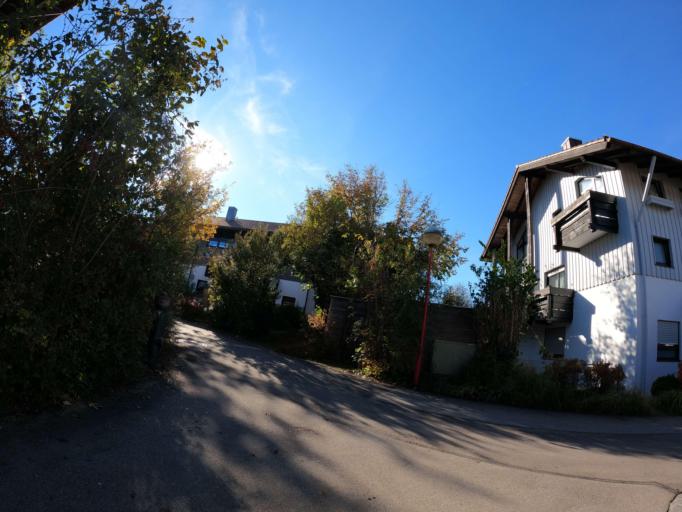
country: DE
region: Bavaria
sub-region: Upper Bavaria
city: Oberhaching
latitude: 48.0255
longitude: 11.5993
